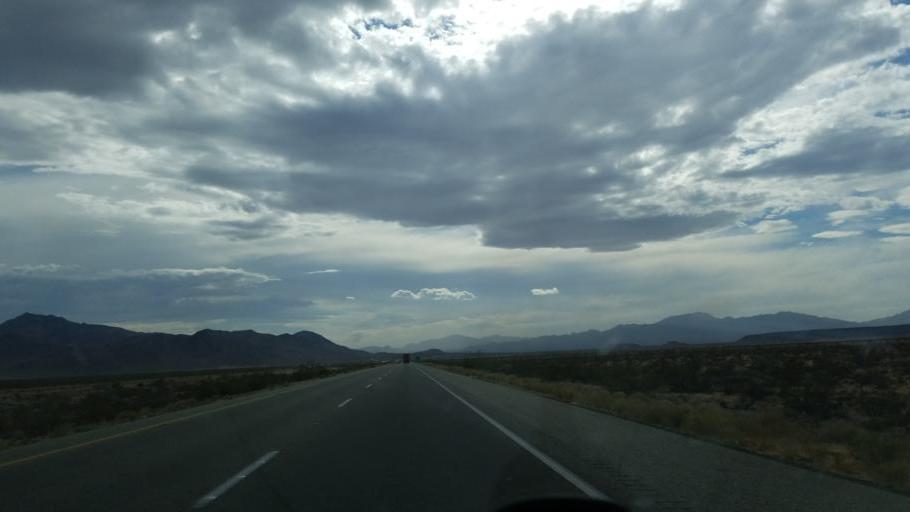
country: US
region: California
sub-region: San Bernardino County
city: Needles
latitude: 34.8040
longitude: -115.2871
